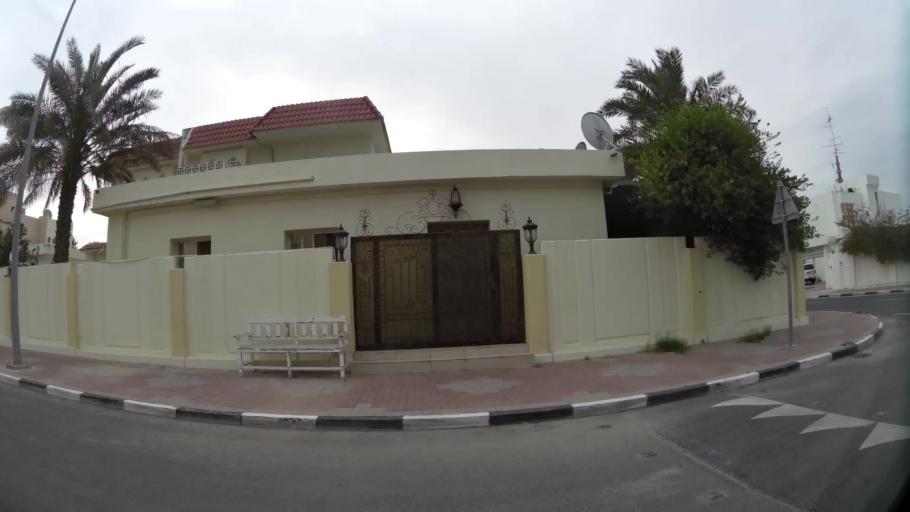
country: QA
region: Baladiyat ad Dawhah
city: Doha
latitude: 25.3278
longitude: 51.5090
